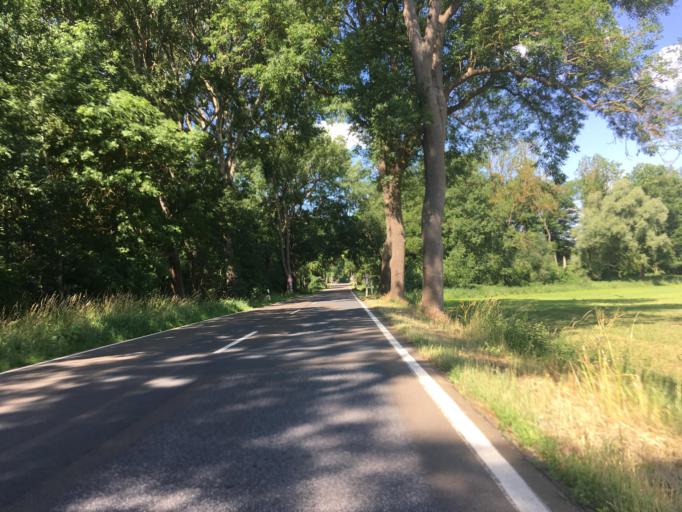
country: DE
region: Brandenburg
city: Goritz
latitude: 53.4423
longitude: 13.9076
